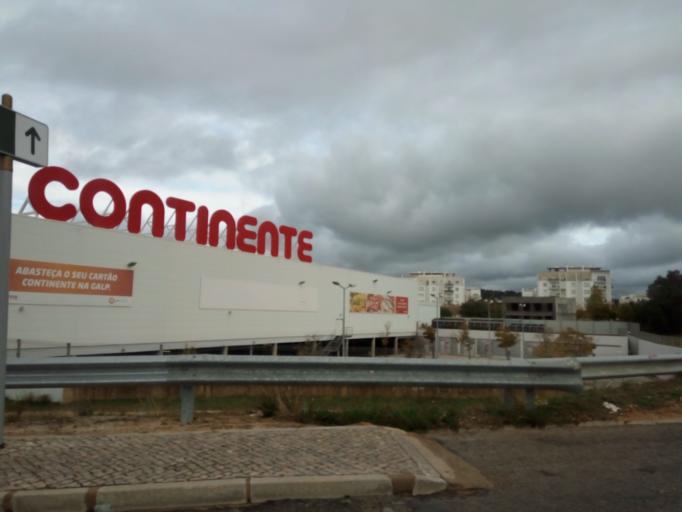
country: PT
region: Faro
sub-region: Loule
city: Loule
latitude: 37.1303
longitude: -8.0047
